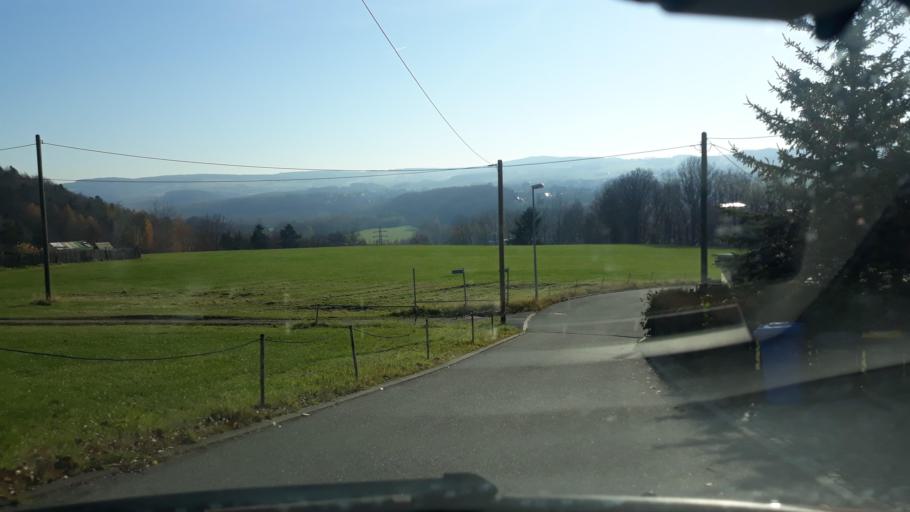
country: DE
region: Saxony
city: Wilkau-Hasslau
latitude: 50.6688
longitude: 12.5526
